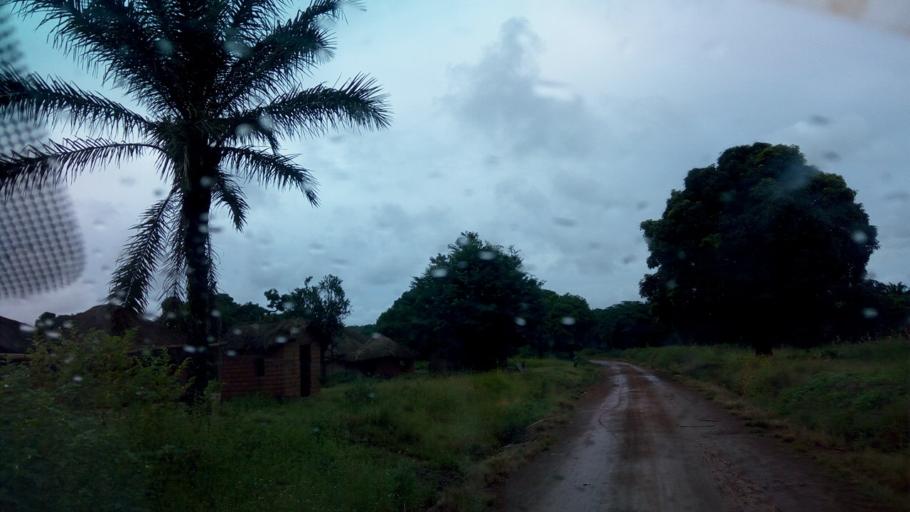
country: ZM
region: Luapula
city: Nchelenge
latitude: -8.9982
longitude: 28.4345
